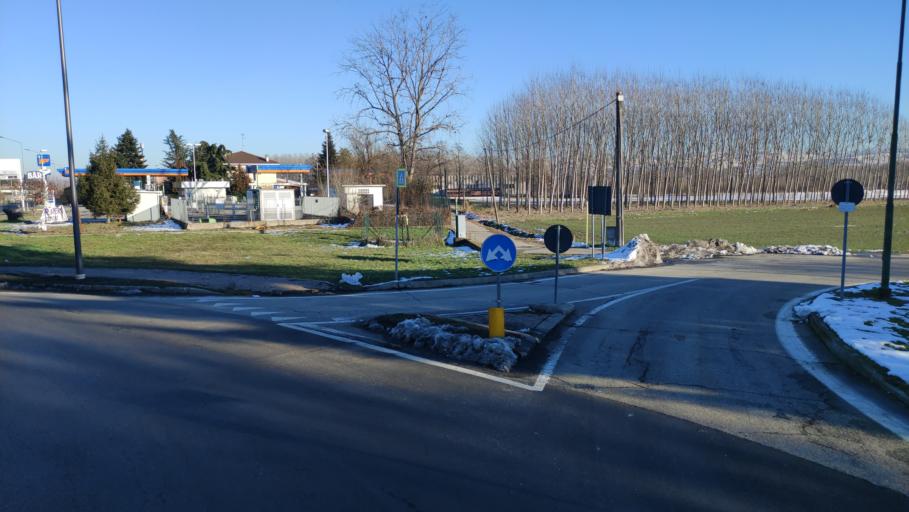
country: IT
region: Piedmont
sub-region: Provincia di Cuneo
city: Borgo
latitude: 44.7041
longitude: 7.9843
